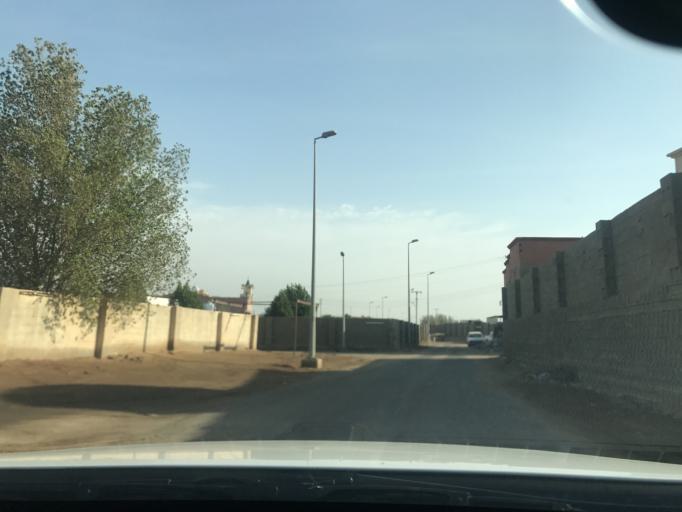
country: SA
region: Makkah
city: Al Jumum
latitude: 21.4531
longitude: 39.5357
